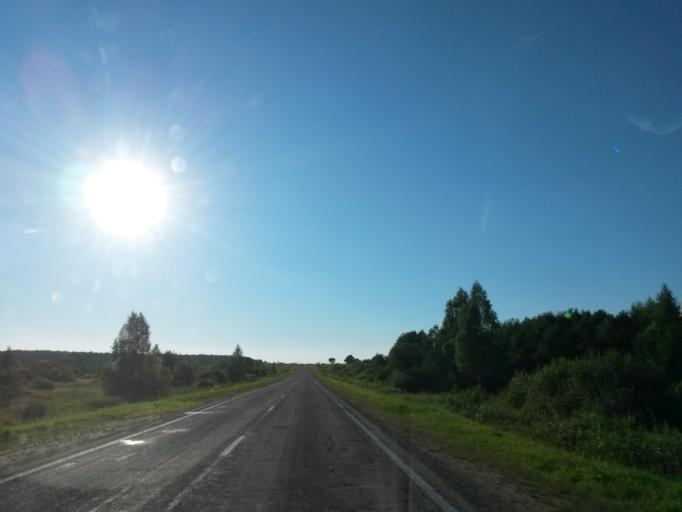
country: RU
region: Jaroslavl
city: Gavrilov-Yam
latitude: 57.2806
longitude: 39.9110
